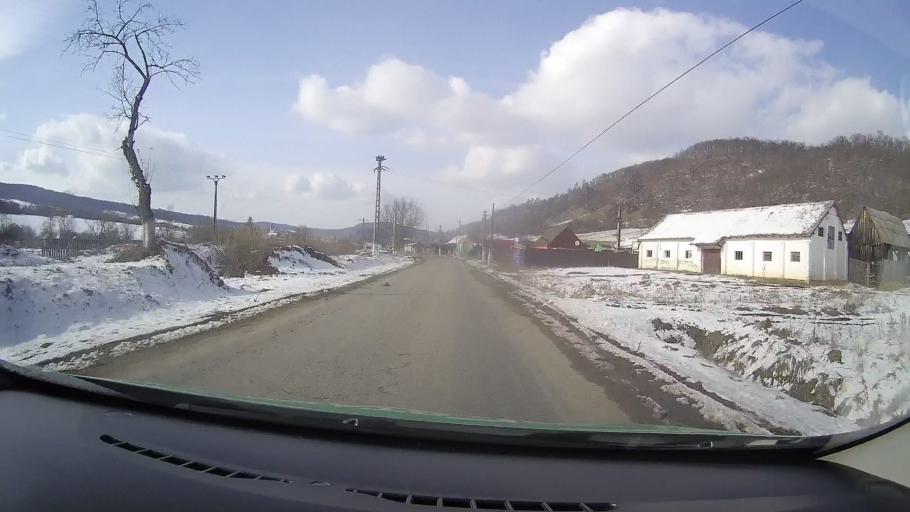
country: RO
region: Sibiu
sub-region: Comuna Iacobeni
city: Iacobeni
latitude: 46.0441
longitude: 24.7274
